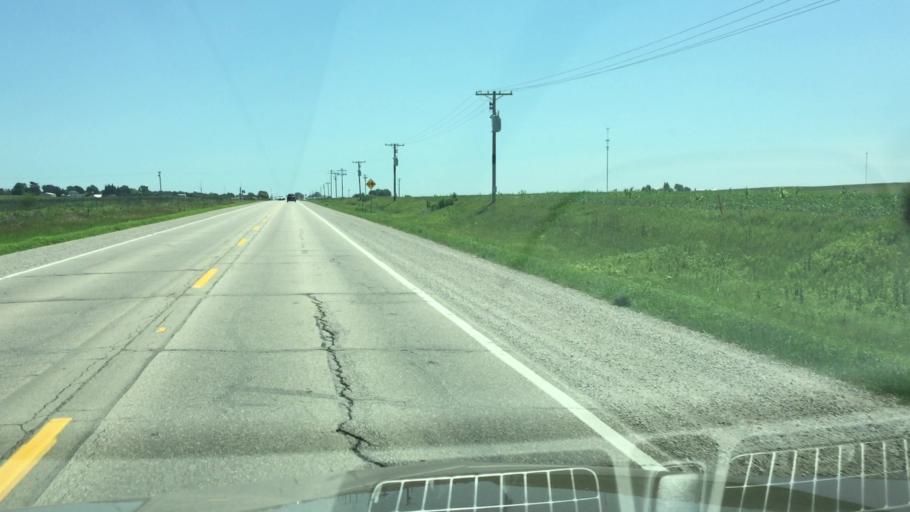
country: US
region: Iowa
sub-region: Cedar County
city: Mechanicsville
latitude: 41.9095
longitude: -91.2830
